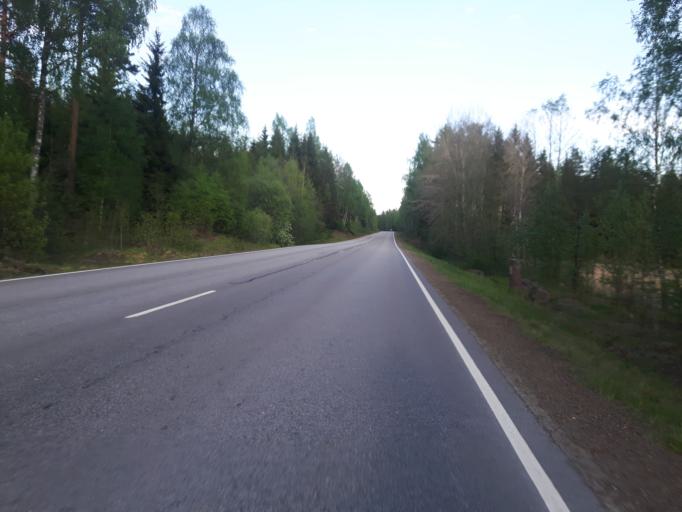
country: FI
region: Uusimaa
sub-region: Loviisa
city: Perna
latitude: 60.4602
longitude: 26.0509
